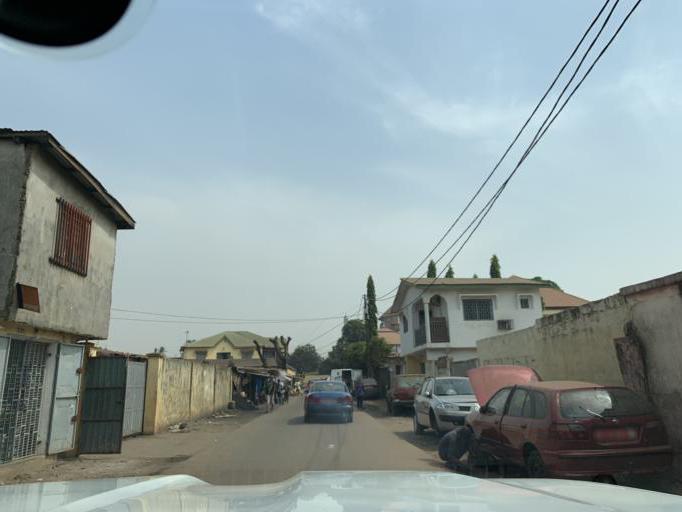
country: GN
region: Conakry
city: Conakry
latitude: 9.5494
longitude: -13.6720
